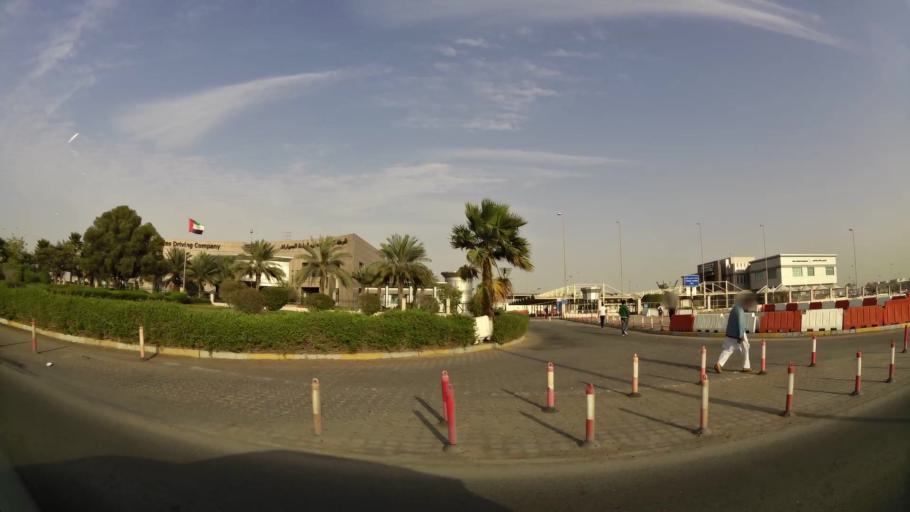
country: AE
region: Abu Dhabi
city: Abu Dhabi
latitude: 24.3435
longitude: 54.5175
